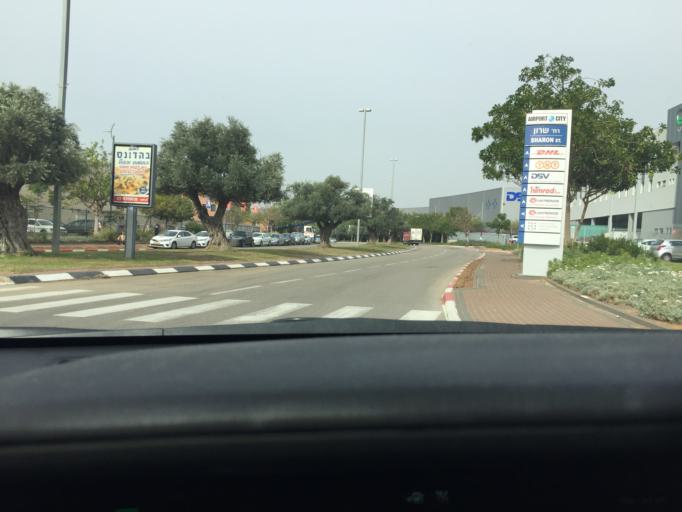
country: IL
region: Central District
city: Lod
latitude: 31.9869
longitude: 34.9160
